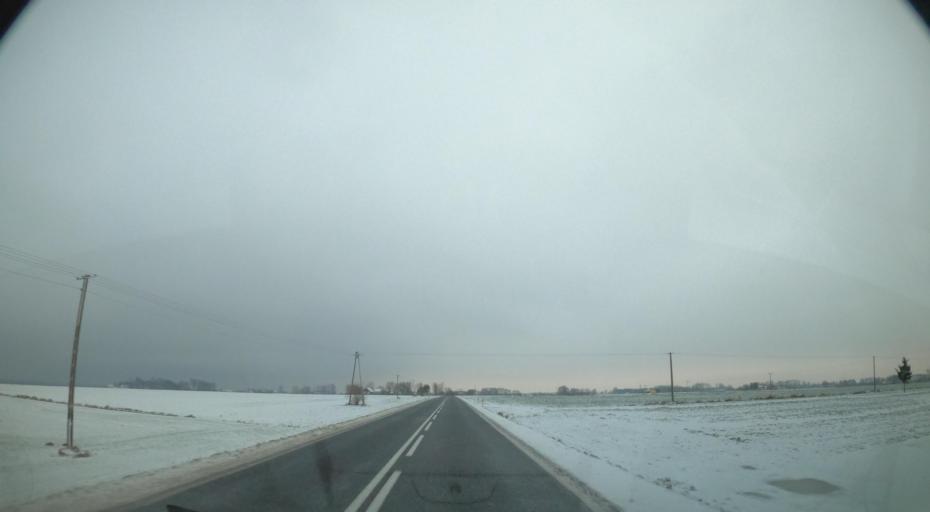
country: PL
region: Masovian Voivodeship
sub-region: Powiat plocki
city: Nowy Duninow
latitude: 52.6270
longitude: 19.4337
